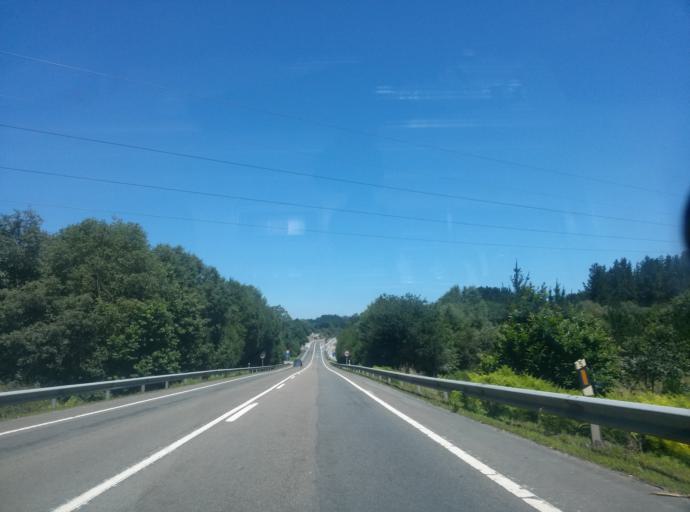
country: ES
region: Galicia
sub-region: Provincia de Lugo
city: Mos
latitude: 43.0880
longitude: -7.4790
